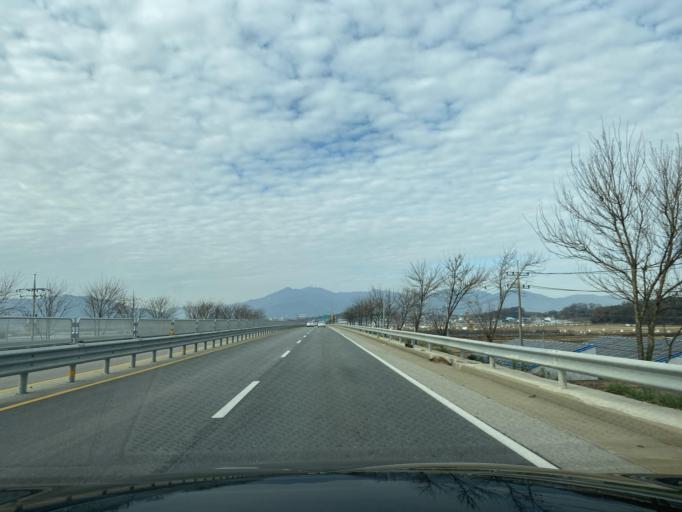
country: KR
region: Chungcheongnam-do
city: Hongsung
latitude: 36.6884
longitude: 126.7132
